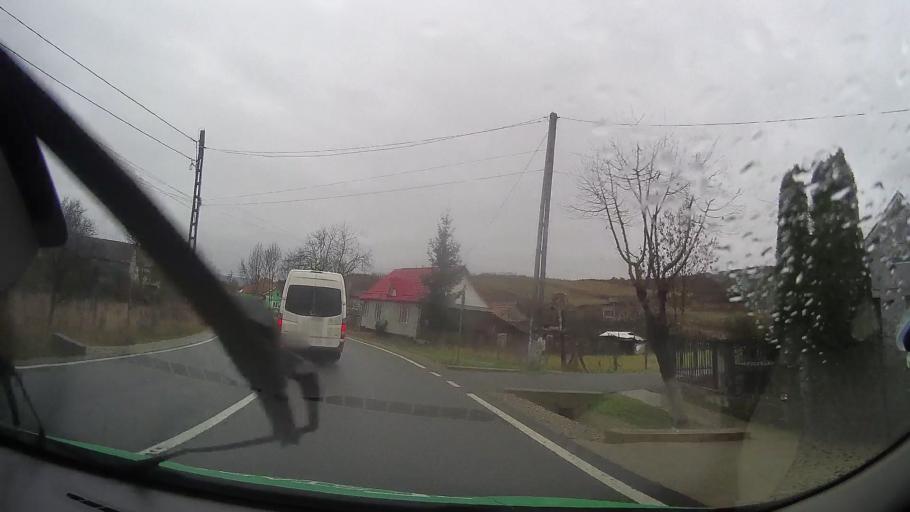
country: RO
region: Bistrita-Nasaud
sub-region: Comuna Galatii Bistritei
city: Galatii Bistritei
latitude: 47.0262
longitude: 24.4161
